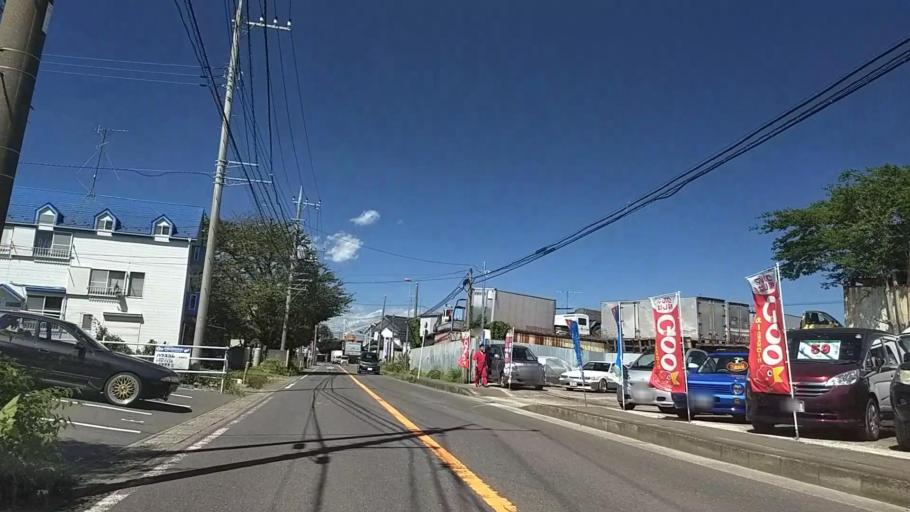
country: JP
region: Kanagawa
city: Zama
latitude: 35.5392
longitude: 139.3440
